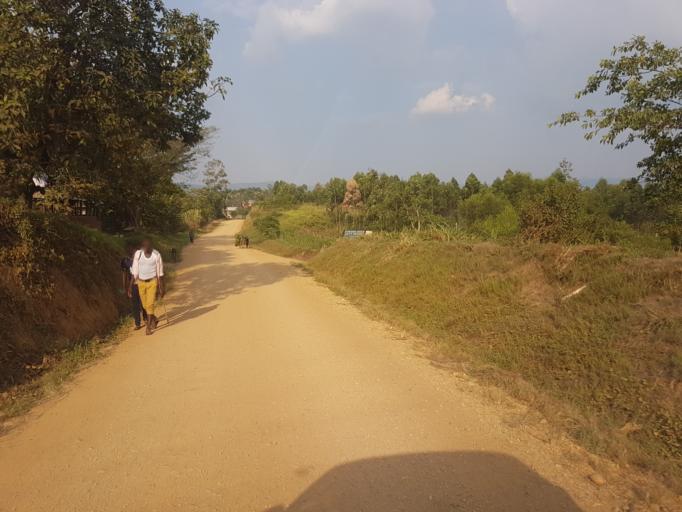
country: UG
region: Western Region
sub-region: Rukungiri District
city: Rukungiri
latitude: -0.6486
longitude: 29.8482
